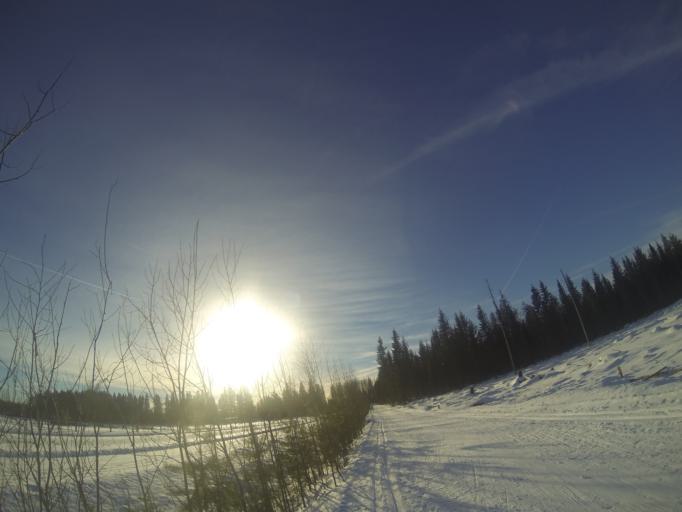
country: FI
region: Southern Savonia
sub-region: Savonlinna
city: Savonlinna
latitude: 61.9201
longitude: 28.9047
